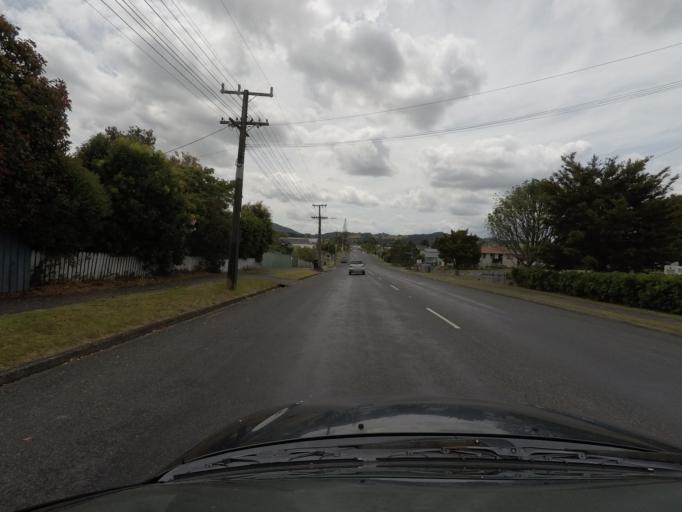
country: NZ
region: Northland
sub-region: Whangarei
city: Whangarei
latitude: -35.6842
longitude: 174.3278
